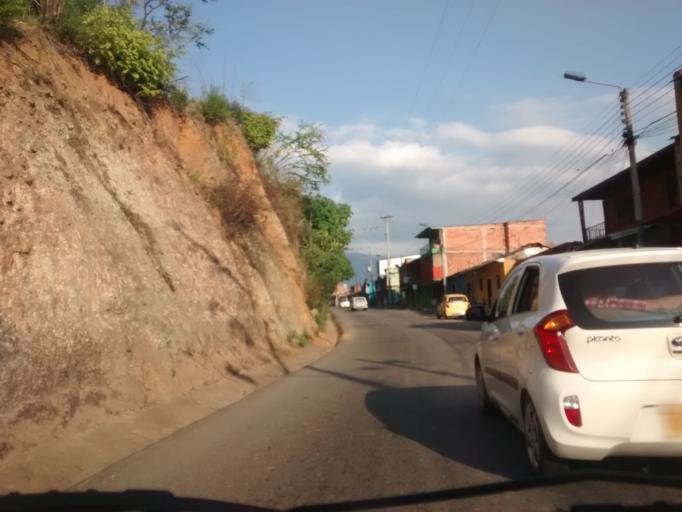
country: CO
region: Santander
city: Bucaramanga
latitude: 7.0948
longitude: -73.1272
